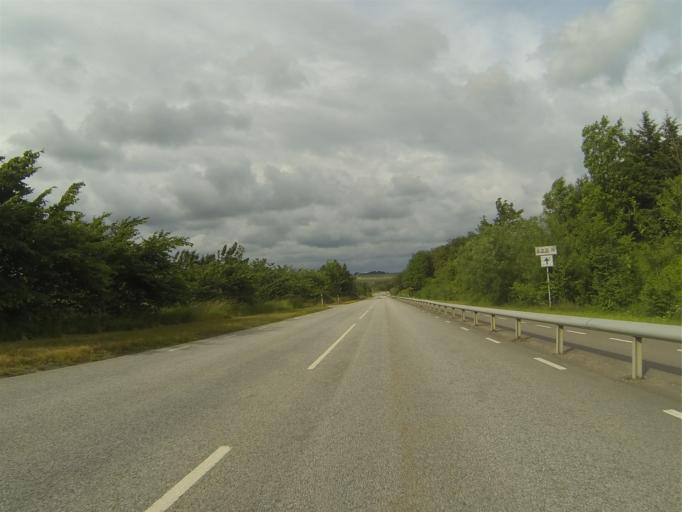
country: SE
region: Skane
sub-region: Eslovs Kommun
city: Eslov
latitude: 55.7612
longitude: 13.3091
